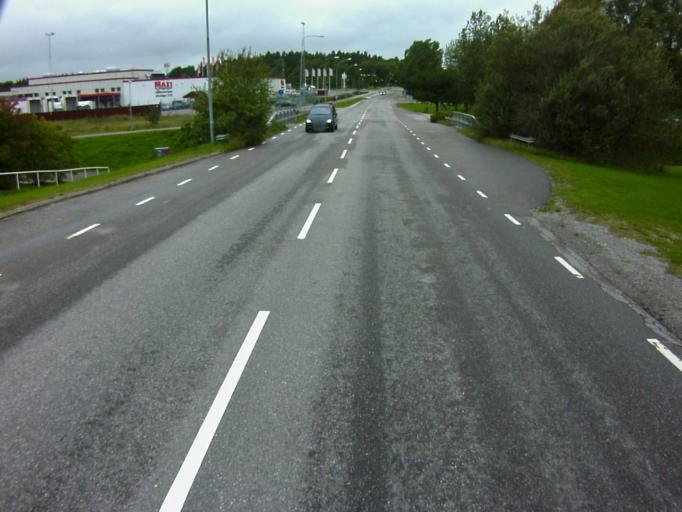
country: SE
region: Soedermanland
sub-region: Eskilstuna Kommun
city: Eskilstuna
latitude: 59.3881
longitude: 16.5383
